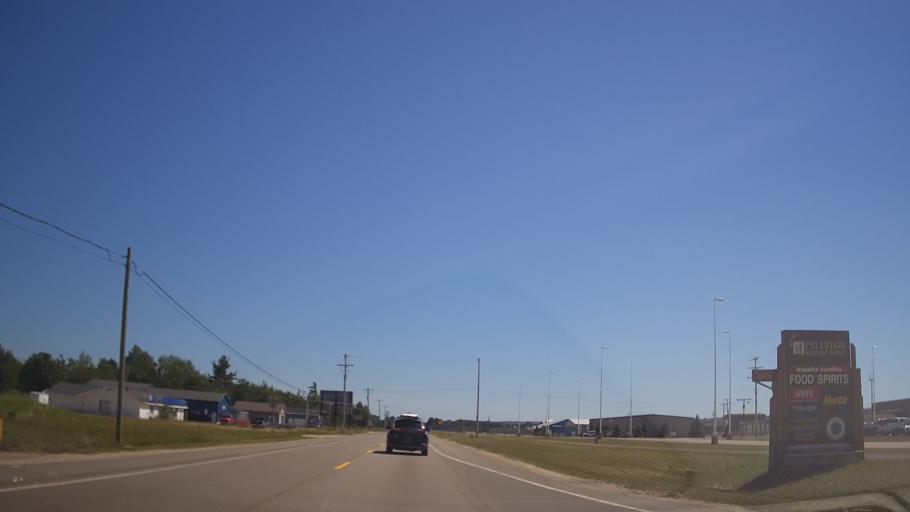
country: US
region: Michigan
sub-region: Cheboygan County
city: Indian River
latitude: 45.5711
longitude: -84.7838
